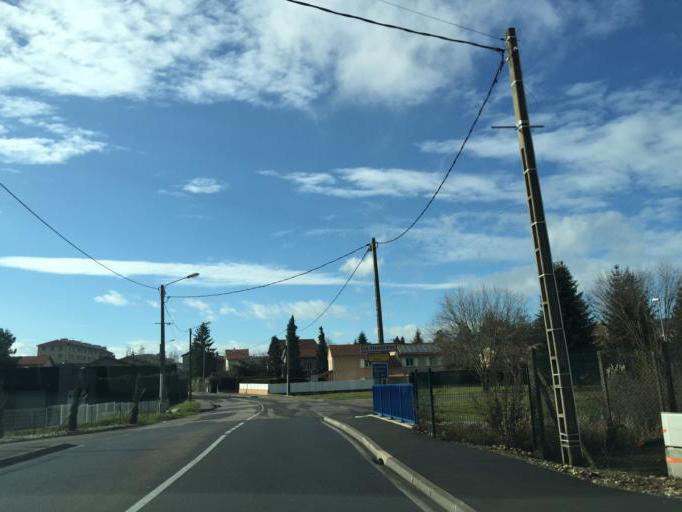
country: FR
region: Rhone-Alpes
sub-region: Departement de la Loire
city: La Talaudiere
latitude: 45.4784
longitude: 4.4411
